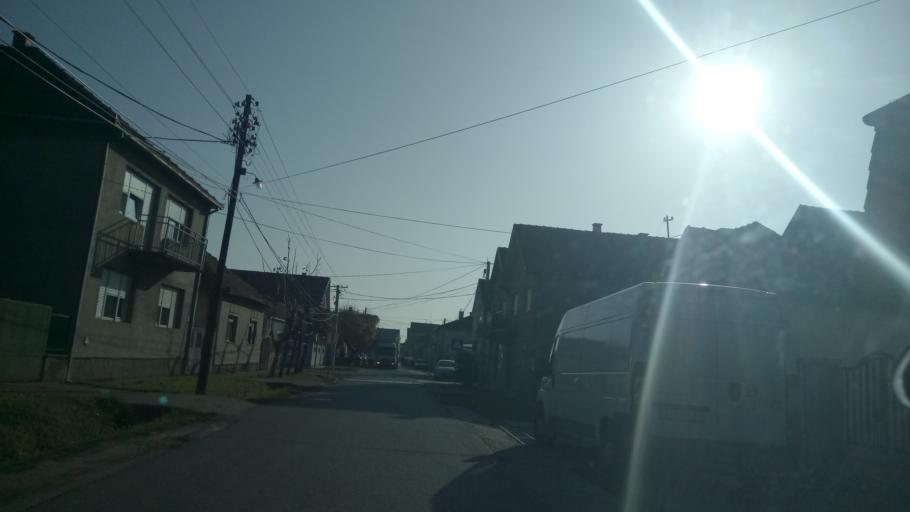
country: RS
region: Autonomna Pokrajina Vojvodina
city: Nova Pazova
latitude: 44.9449
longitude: 20.2145
